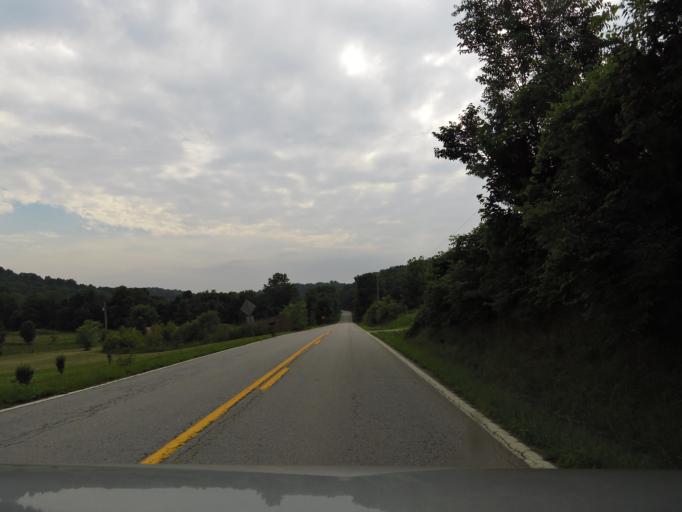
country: US
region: Kentucky
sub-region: Harrison County
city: Cynthiana
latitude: 38.5114
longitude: -84.2015
